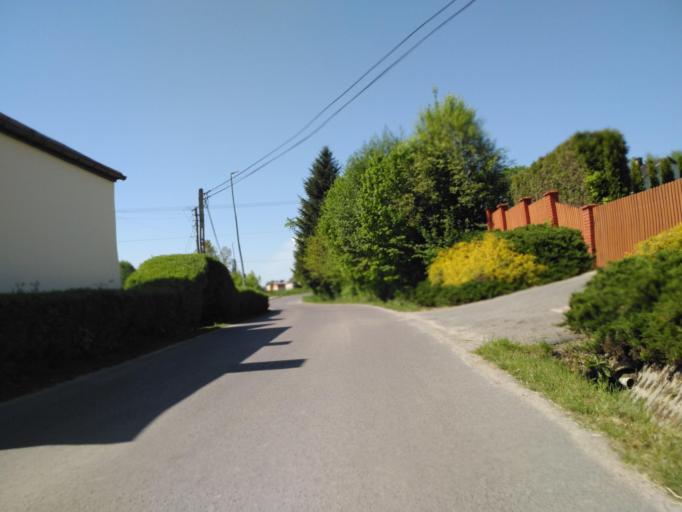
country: PL
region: Subcarpathian Voivodeship
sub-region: Powiat krosnienski
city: Korczyna
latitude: 49.7217
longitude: 21.8143
